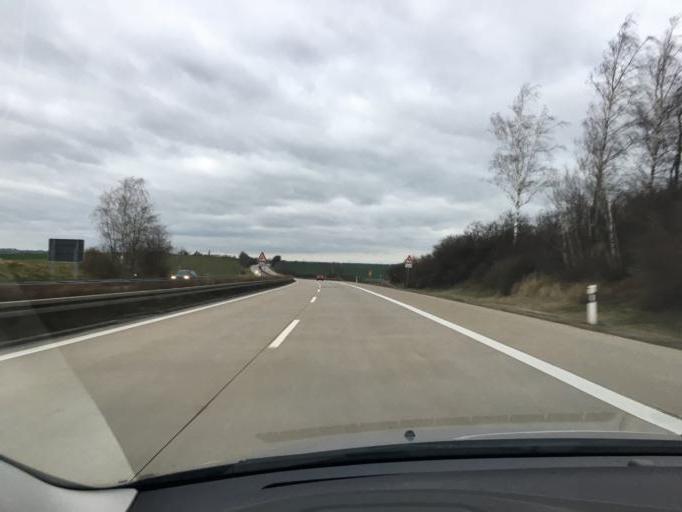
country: DE
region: Saxony
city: Mochau
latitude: 51.1299
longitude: 13.1649
